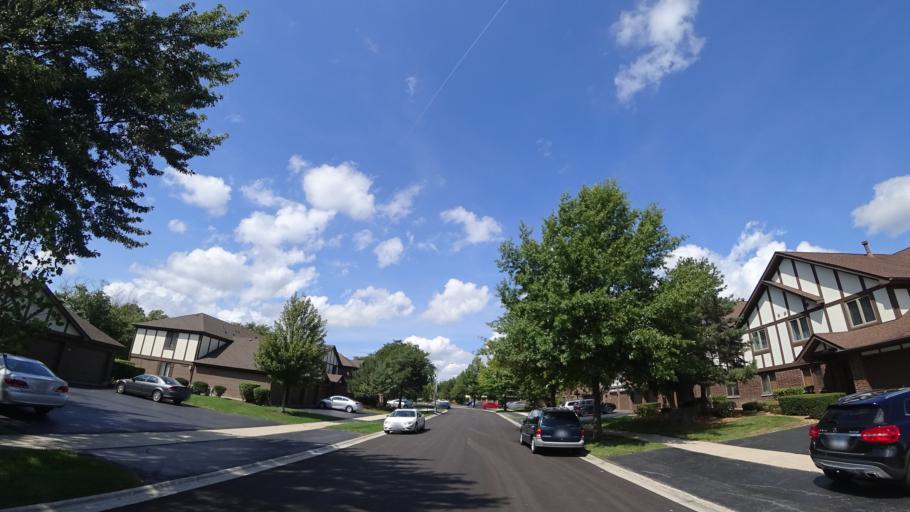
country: US
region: Illinois
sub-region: Cook County
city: Tinley Park
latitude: 41.5638
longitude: -87.7820
